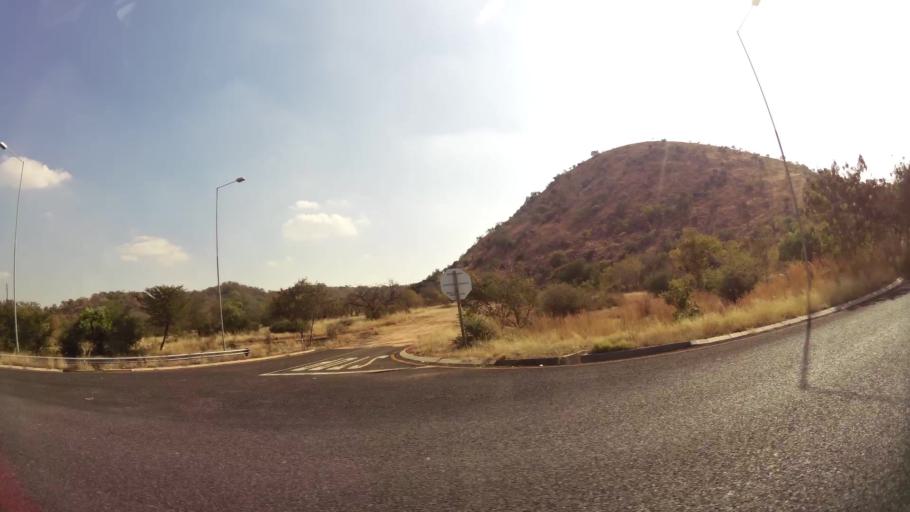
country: ZA
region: North-West
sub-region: Bojanala Platinum District Municipality
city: Rustenburg
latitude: -25.5767
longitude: 27.1385
